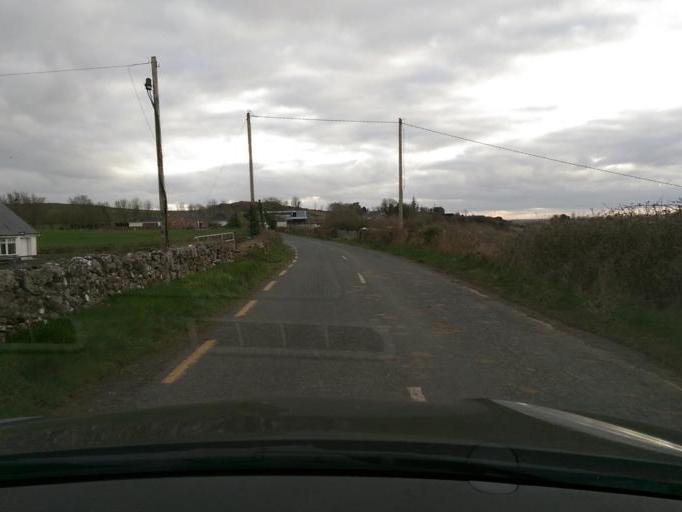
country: IE
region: Leinster
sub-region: Uibh Fhaili
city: Banagher
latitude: 53.3141
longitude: -7.9998
